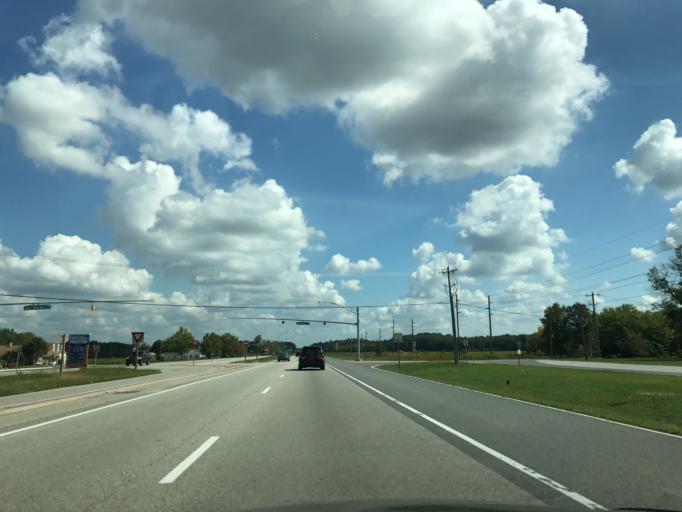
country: US
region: Maryland
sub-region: Queen Anne's County
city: Grasonville
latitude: 38.9872
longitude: -76.1541
